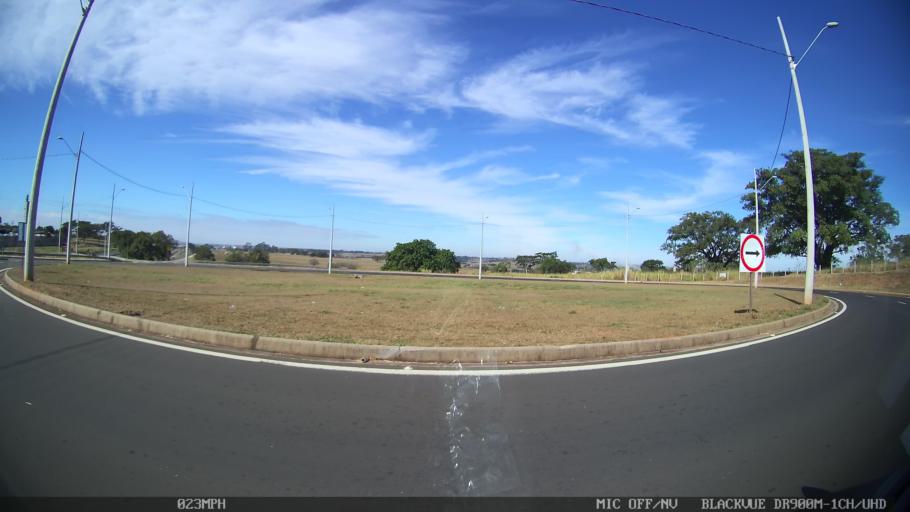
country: BR
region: Sao Paulo
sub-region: Sao Jose Do Rio Preto
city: Sao Jose do Rio Preto
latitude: -20.8513
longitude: -49.3929
